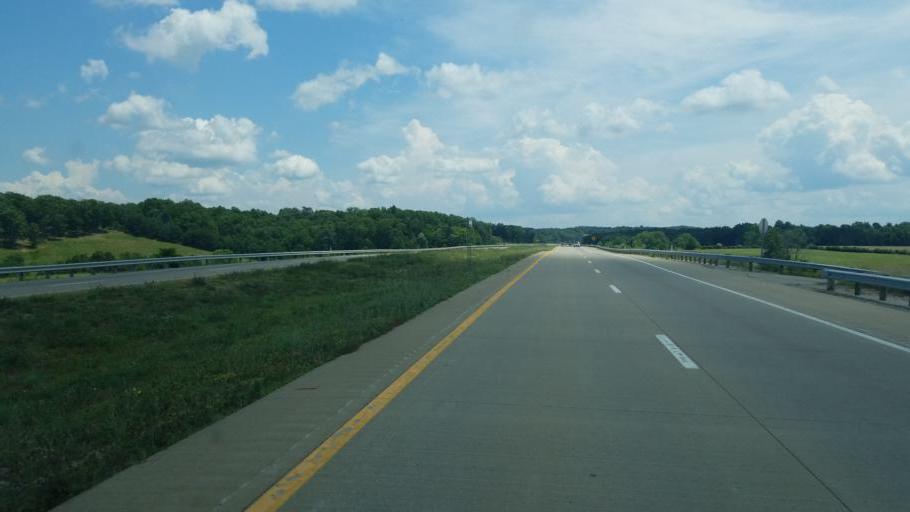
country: US
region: West Virginia
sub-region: Mason County
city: Point Pleasant
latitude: 38.7667
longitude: -82.0273
